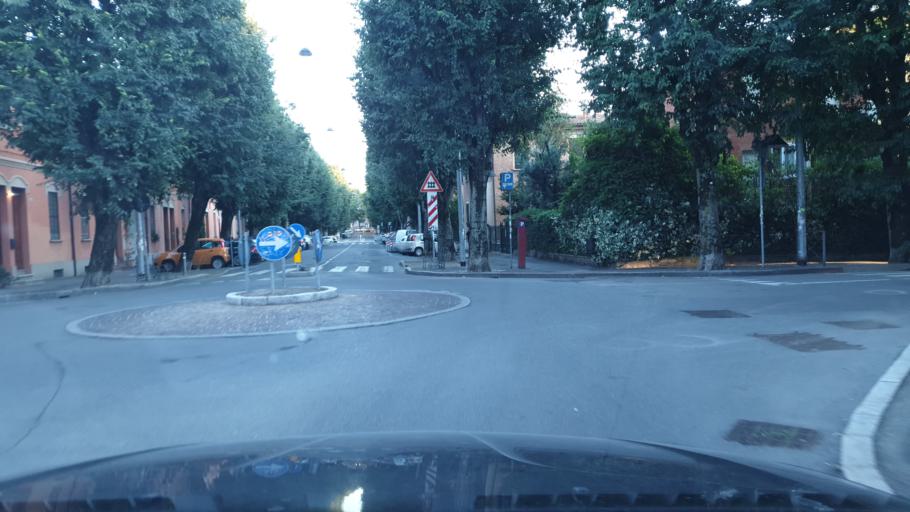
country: IT
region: Emilia-Romagna
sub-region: Provincia di Bologna
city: Bologna
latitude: 44.4954
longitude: 11.3626
